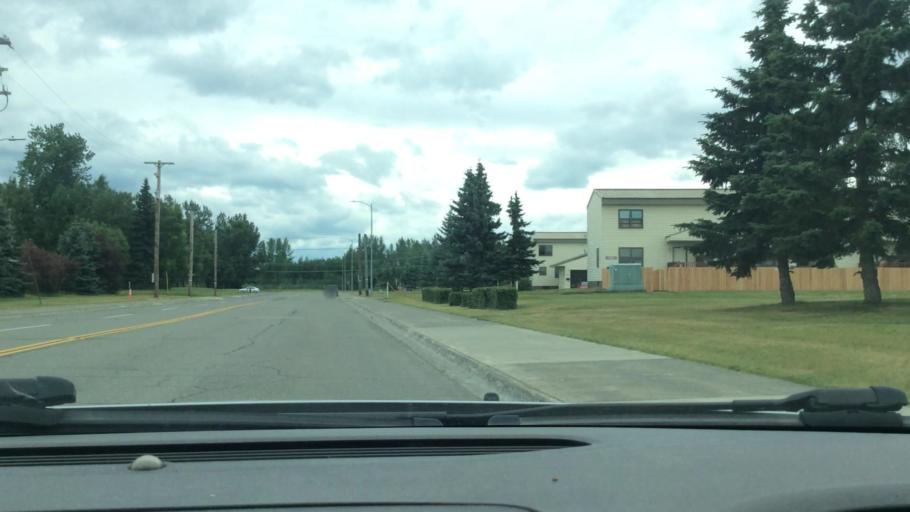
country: US
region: Alaska
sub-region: Anchorage Municipality
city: Anchorage
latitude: 61.2311
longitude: -149.8493
